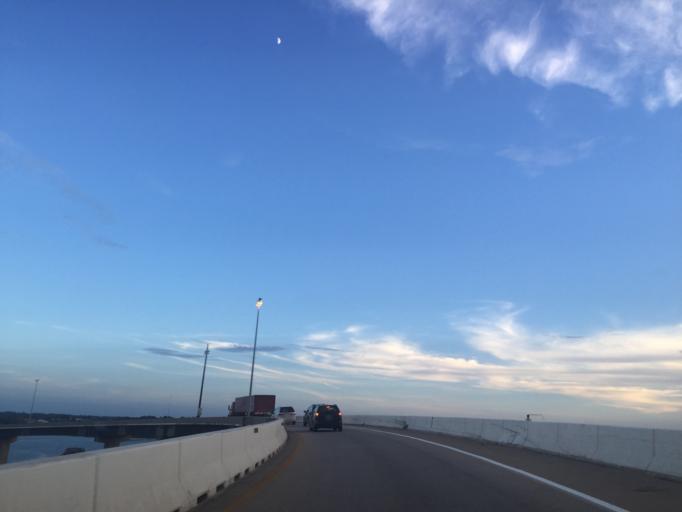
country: US
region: Maryland
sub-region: City of Baltimore
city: Baltimore
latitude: 39.2693
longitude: -76.6242
